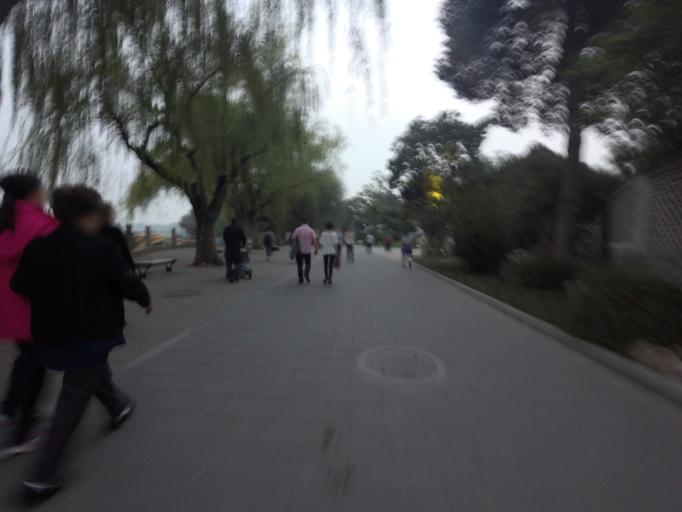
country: CN
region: Beijing
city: Jingshan
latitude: 39.9312
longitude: 116.3835
